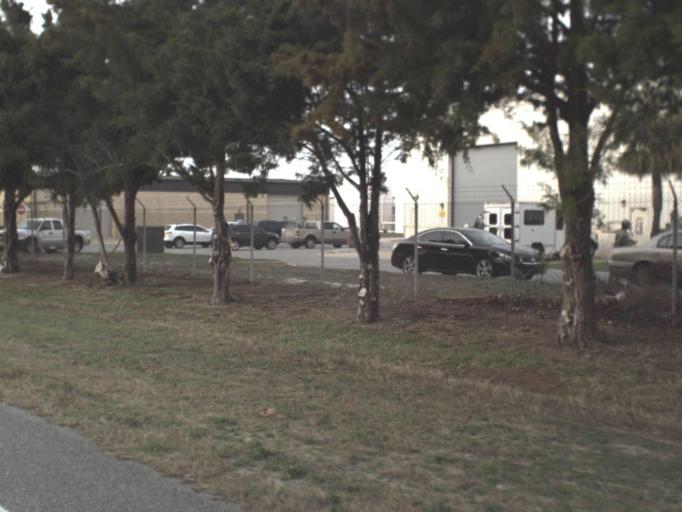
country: US
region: Florida
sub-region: Bay County
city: Tyndall Air Force Base
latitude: 30.0644
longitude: -85.5829
